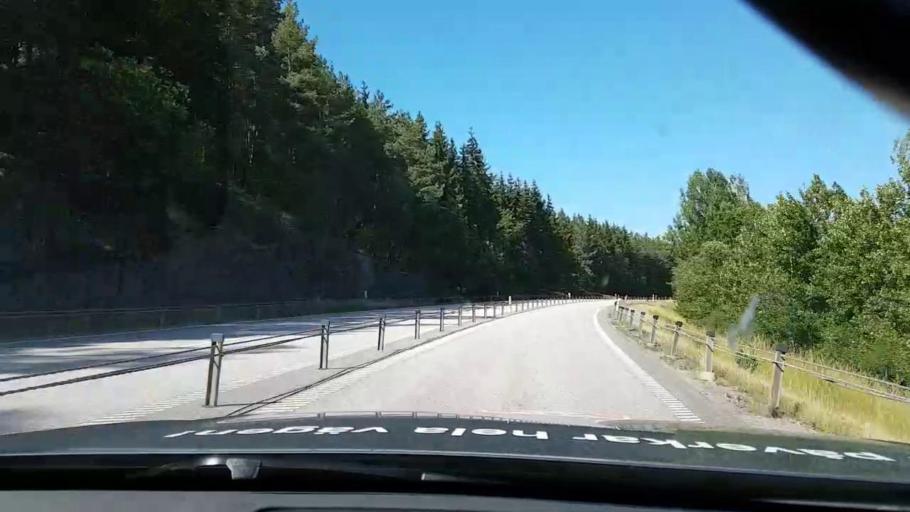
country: SE
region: Kalmar
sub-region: Vasterviks Kommun
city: Gamleby
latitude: 57.9274
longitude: 16.3975
